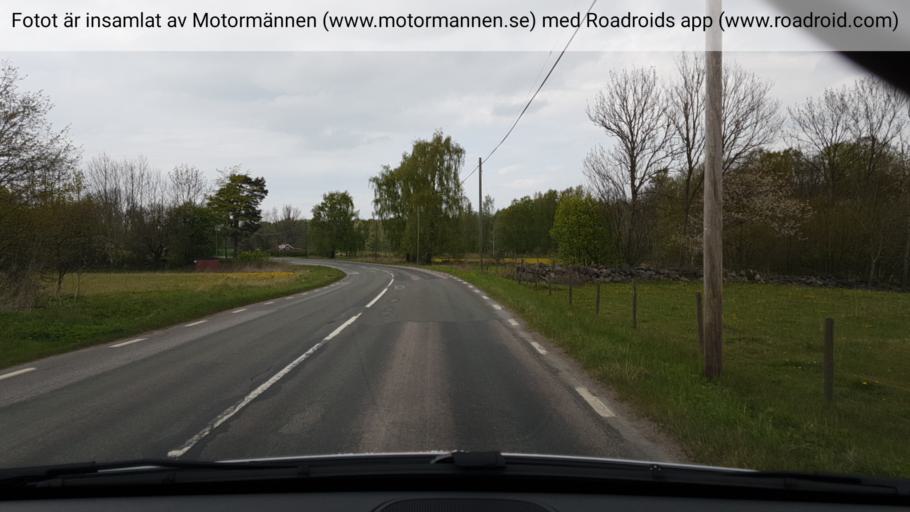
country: SE
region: Vaestra Goetaland
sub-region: Skovde Kommun
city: Stopen
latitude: 58.4877
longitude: 13.8355
